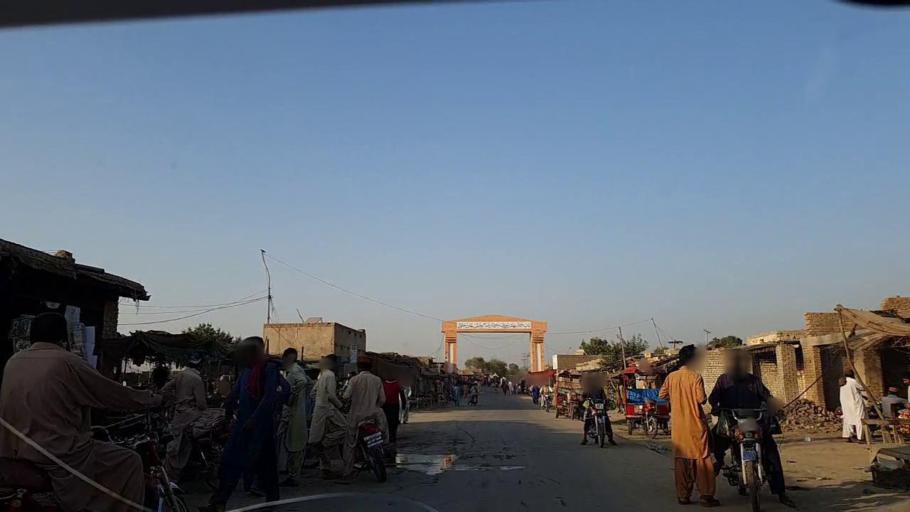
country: PK
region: Sindh
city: Rustam jo Goth
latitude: 28.0207
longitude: 68.8123
